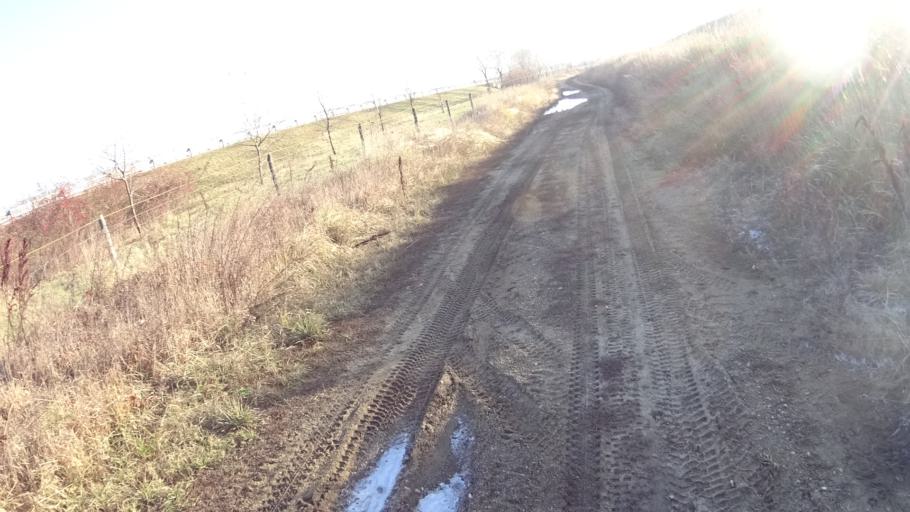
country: HU
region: Borsod-Abauj-Zemplen
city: Onod
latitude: 47.9851
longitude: 20.8964
